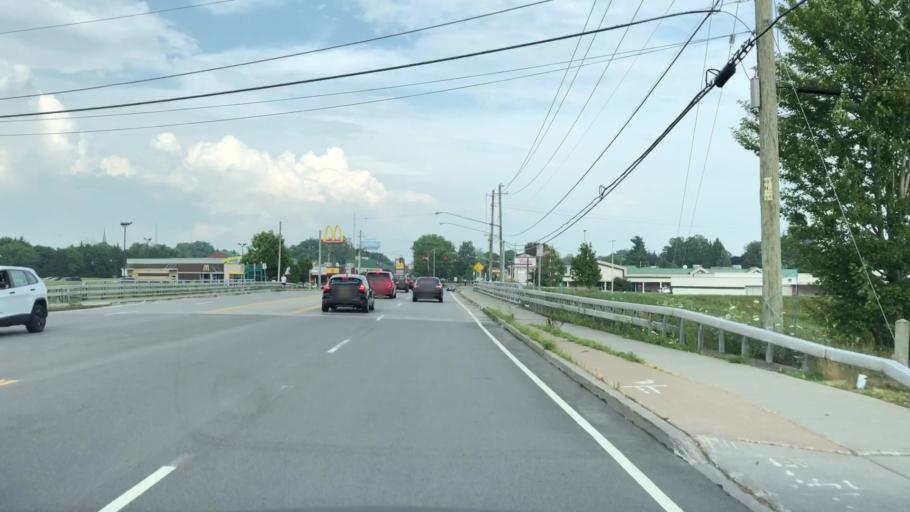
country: US
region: New York
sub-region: Erie County
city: Depew
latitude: 42.9014
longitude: -78.6856
